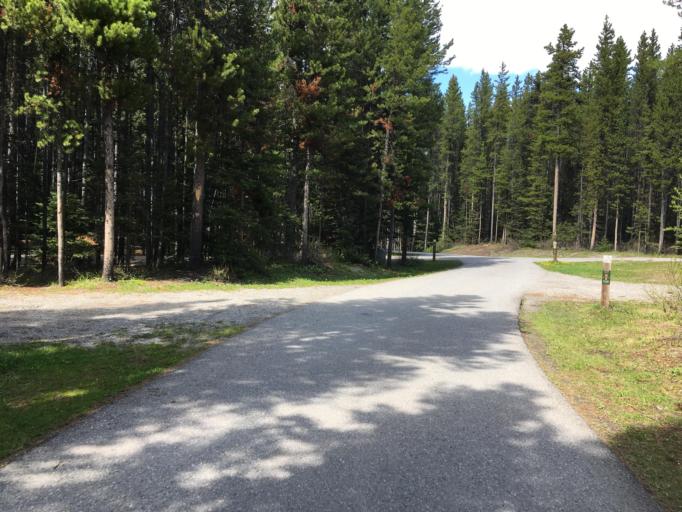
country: CA
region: Alberta
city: Canmore
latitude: 50.6271
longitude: -115.0998
